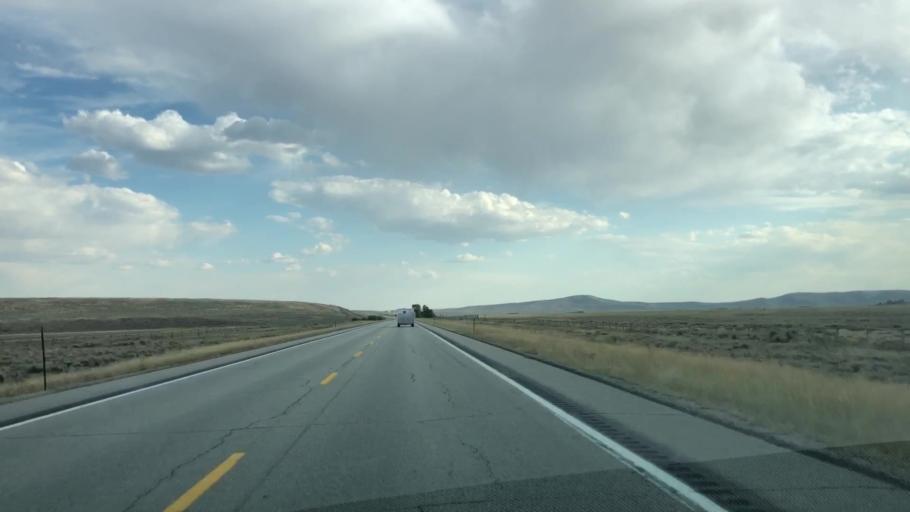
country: US
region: Wyoming
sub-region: Sublette County
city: Pinedale
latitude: 42.9588
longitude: -110.0876
